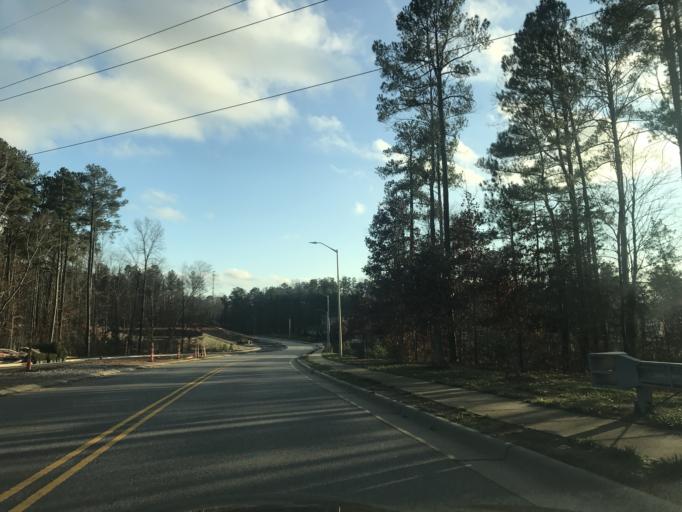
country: US
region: North Carolina
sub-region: Wake County
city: Wake Forest
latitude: 35.9585
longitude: -78.5339
